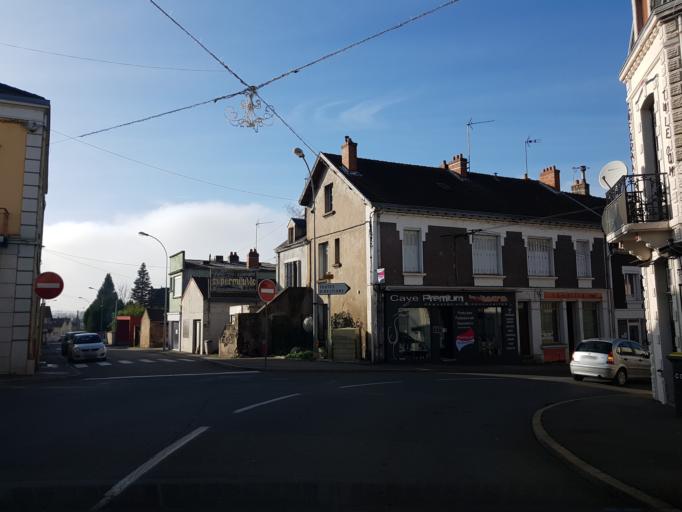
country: FR
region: Bourgogne
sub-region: Departement de Saone-et-Loire
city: Gueugnon
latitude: 46.6002
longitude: 4.0662
